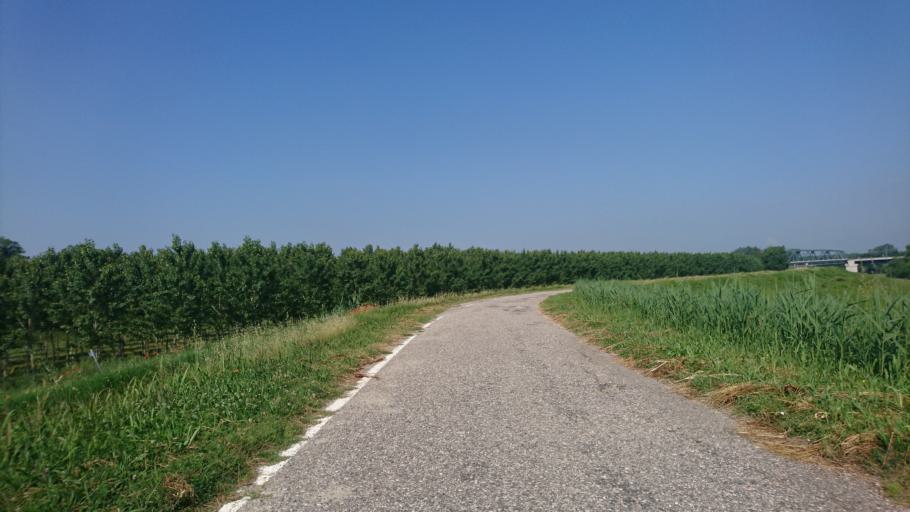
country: IT
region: Lombardy
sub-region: Provincia di Mantova
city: Revere
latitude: 45.0550
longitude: 11.1454
